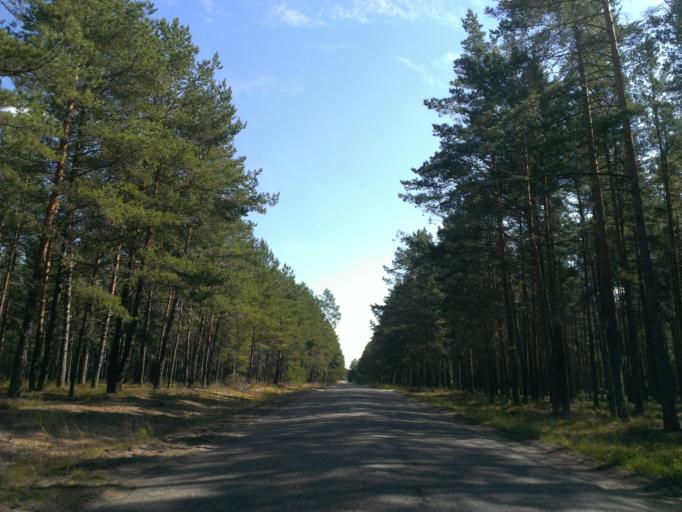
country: LV
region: Adazi
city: Adazi
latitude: 57.1038
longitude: 24.3826
